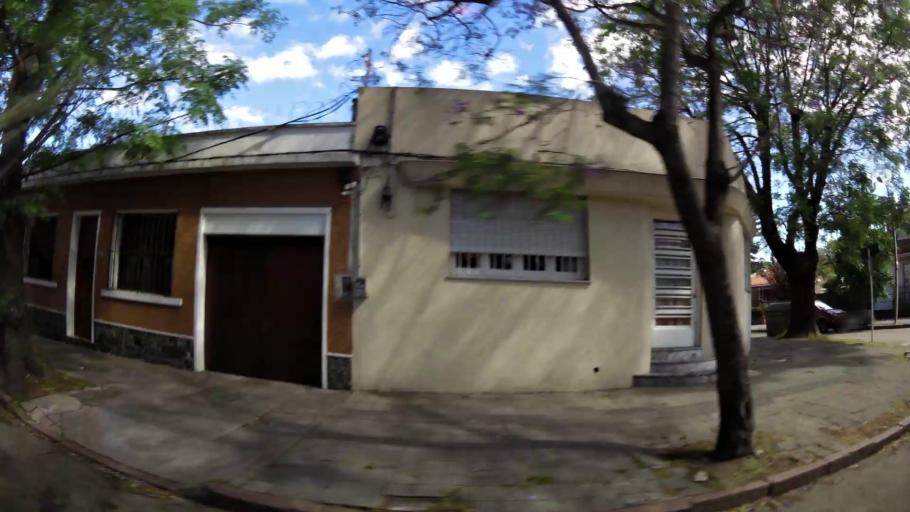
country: UY
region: Montevideo
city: Montevideo
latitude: -34.8609
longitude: -56.1954
